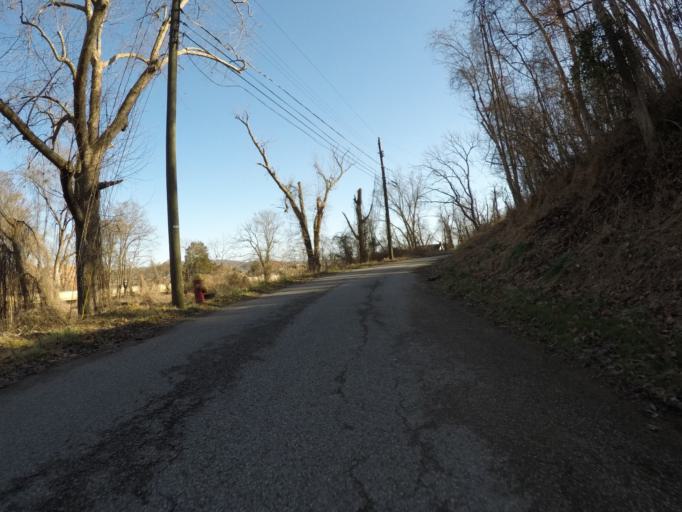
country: US
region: Kentucky
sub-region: Boyd County
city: Catlettsburg
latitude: 38.4192
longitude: -82.6020
